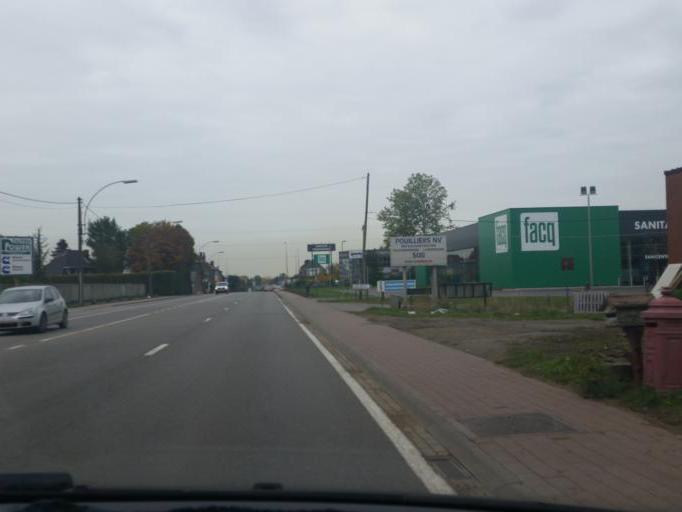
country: BE
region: Flanders
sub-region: Provincie Vlaams-Brabant
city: Halle
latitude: 50.7527
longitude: 4.2471
